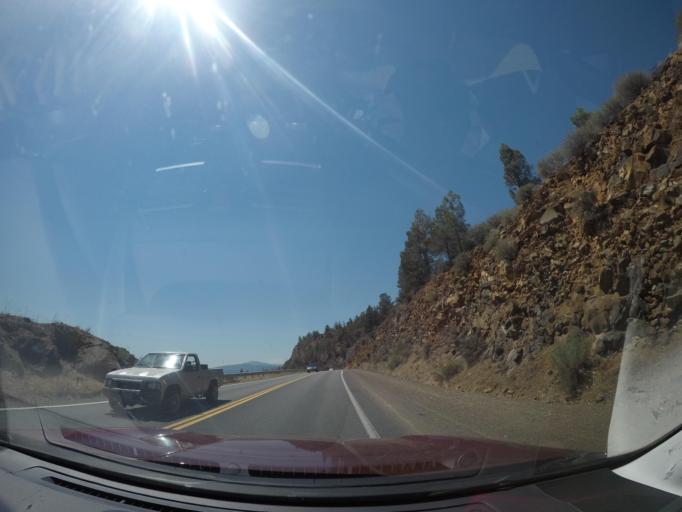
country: US
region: California
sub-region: Shasta County
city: Burney
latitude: 40.9926
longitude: -121.4770
